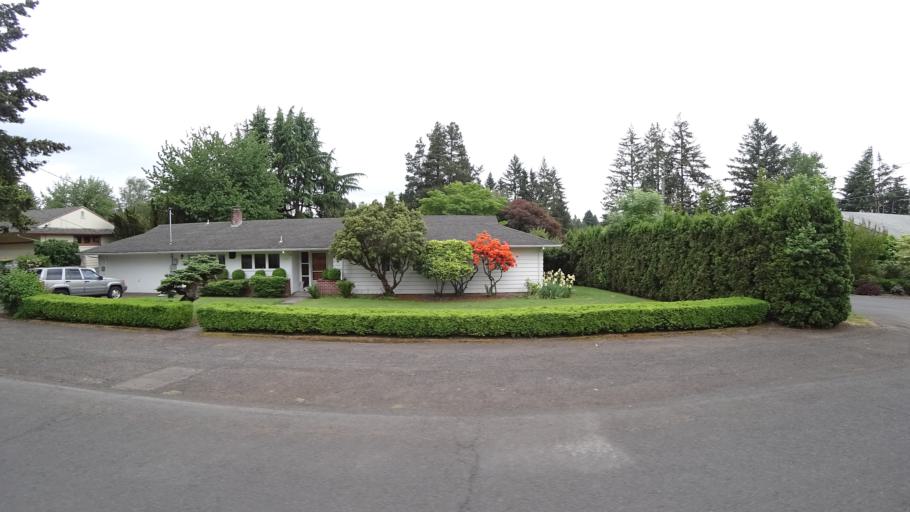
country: US
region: Oregon
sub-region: Washington County
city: Garden Home-Whitford
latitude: 45.4743
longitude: -122.7466
